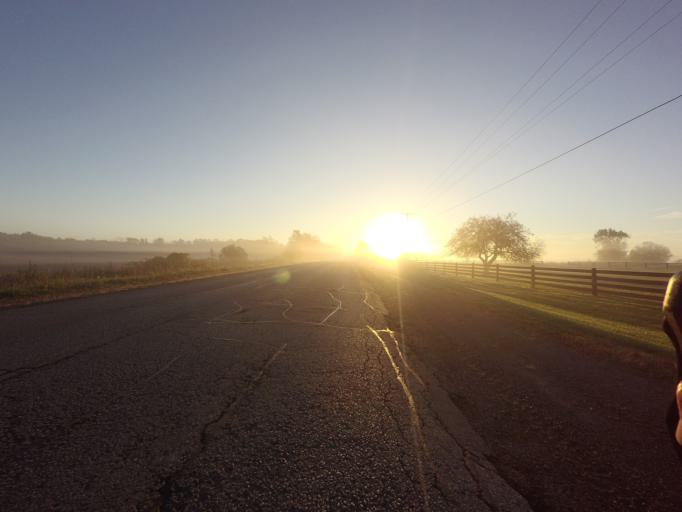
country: CA
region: Ontario
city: Quinte West
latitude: 44.0406
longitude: -77.6144
